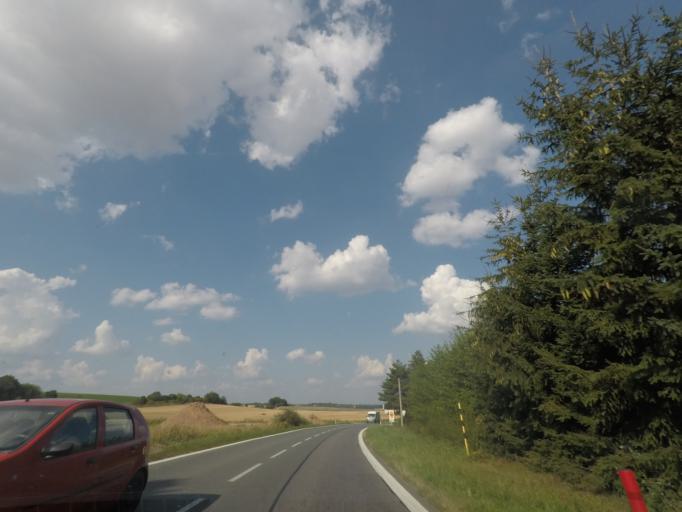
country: CZ
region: Kralovehradecky
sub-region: Okres Nachod
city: Jaromer
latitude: 50.3710
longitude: 15.9070
